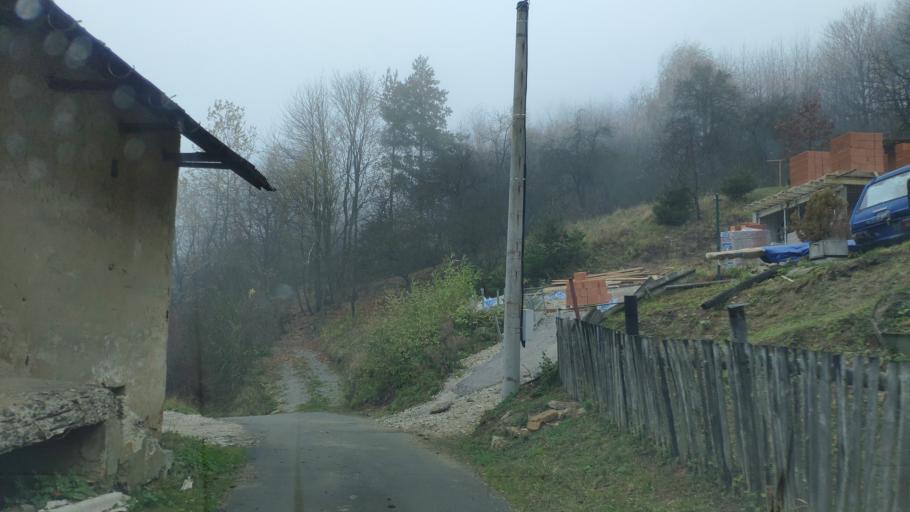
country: SK
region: Presovsky
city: Sabinov
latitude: 49.1401
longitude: 21.2229
